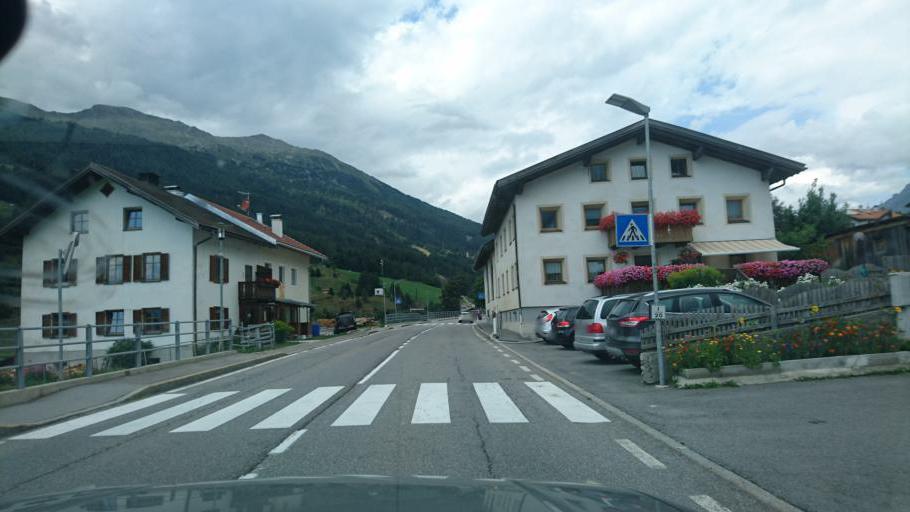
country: IT
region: Trentino-Alto Adige
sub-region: Bolzano
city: Curon Venosta
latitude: 46.7607
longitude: 10.5353
